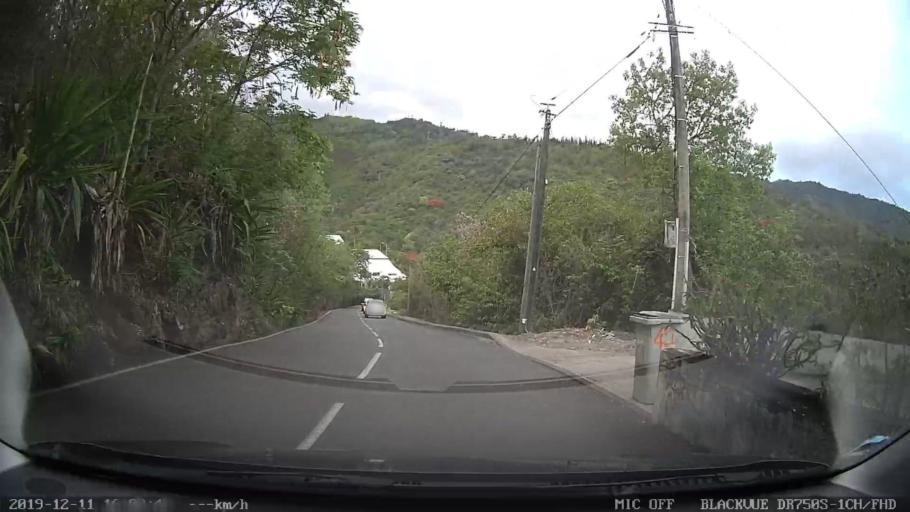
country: RE
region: Reunion
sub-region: Reunion
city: Saint-Denis
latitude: -20.9026
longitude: 55.4579
